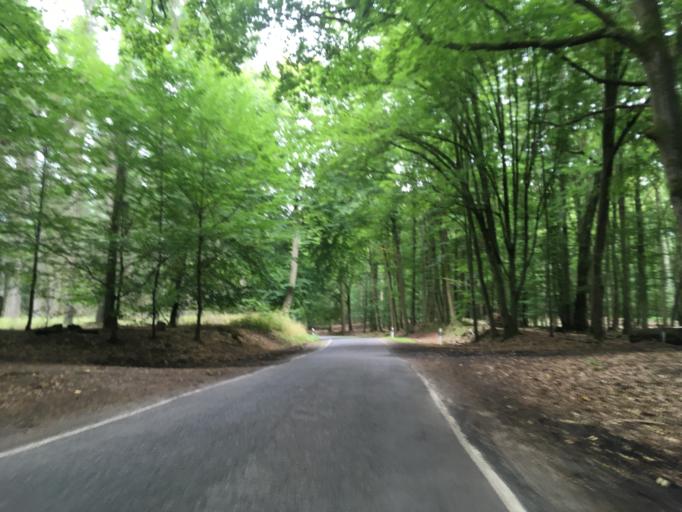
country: DE
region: Brandenburg
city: Althuttendorf
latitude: 53.0532
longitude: 13.8843
